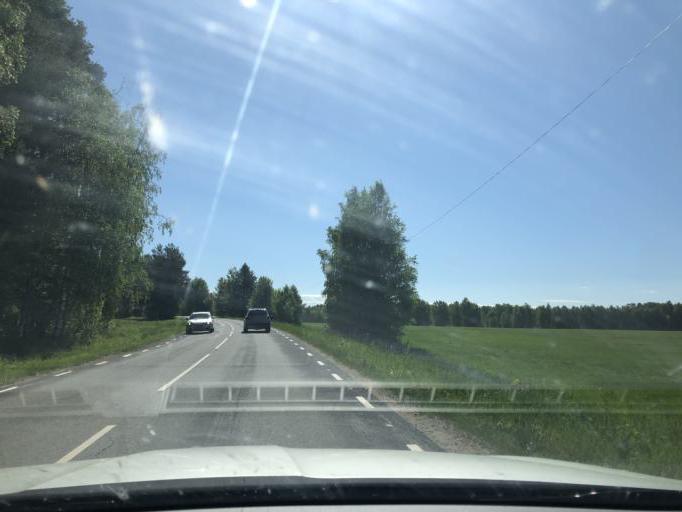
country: SE
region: Norrbotten
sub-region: Lulea Kommun
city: Gammelstad
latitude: 65.6581
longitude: 21.9960
